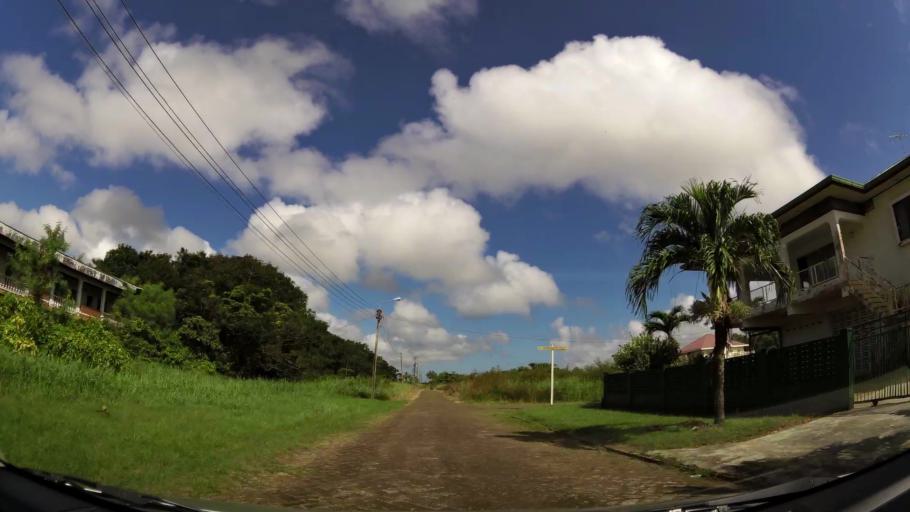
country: SR
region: Commewijne
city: Nieuw Amsterdam
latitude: 5.8778
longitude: -55.1119
